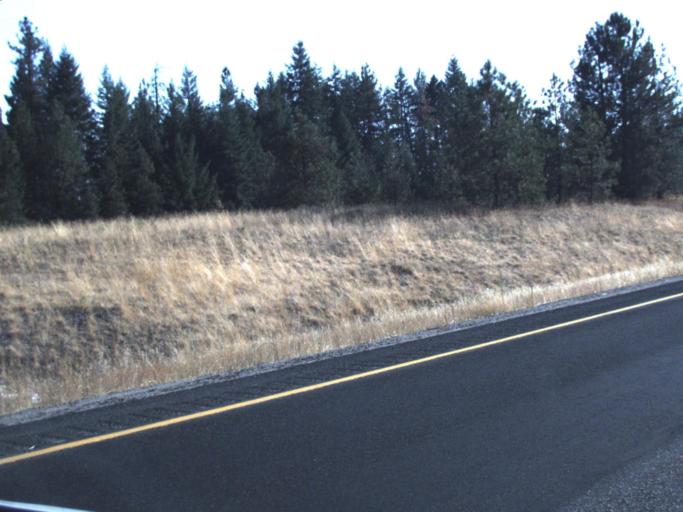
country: US
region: Washington
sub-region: Spokane County
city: Deer Park
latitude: 48.0682
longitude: -117.3370
